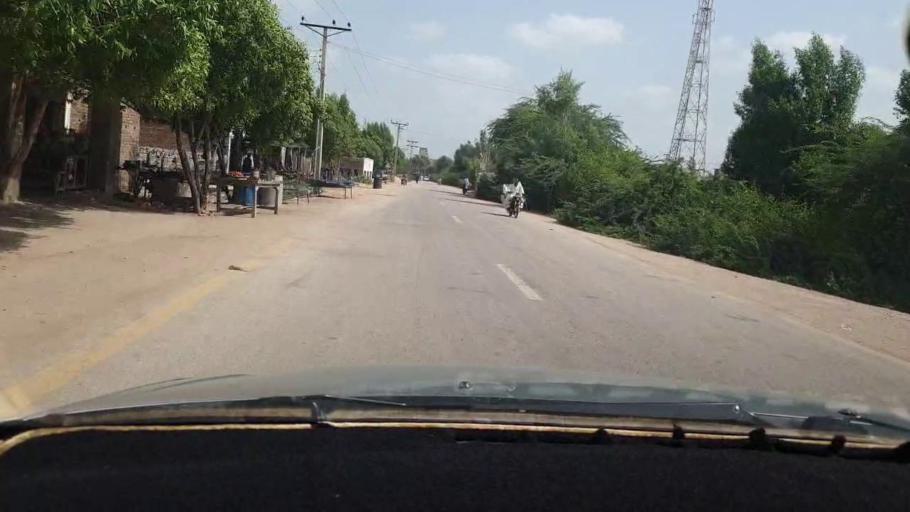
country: PK
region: Sindh
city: Digri
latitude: 25.0759
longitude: 69.2120
